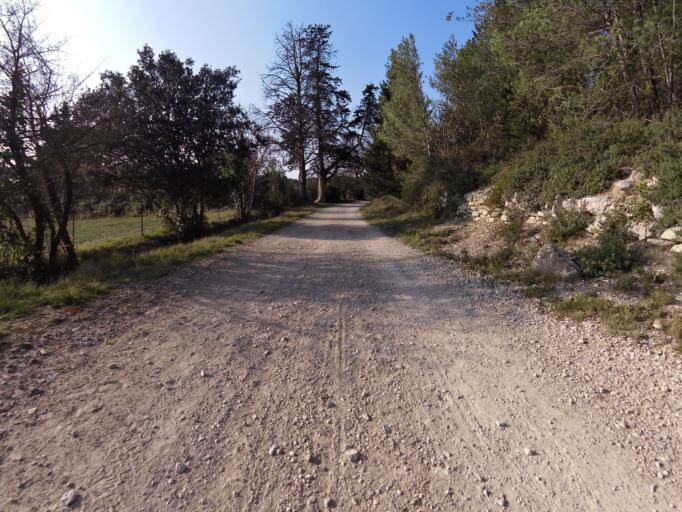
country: FR
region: Languedoc-Roussillon
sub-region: Departement du Gard
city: Gallargues-le-Montueux
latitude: 43.7356
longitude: 4.1595
